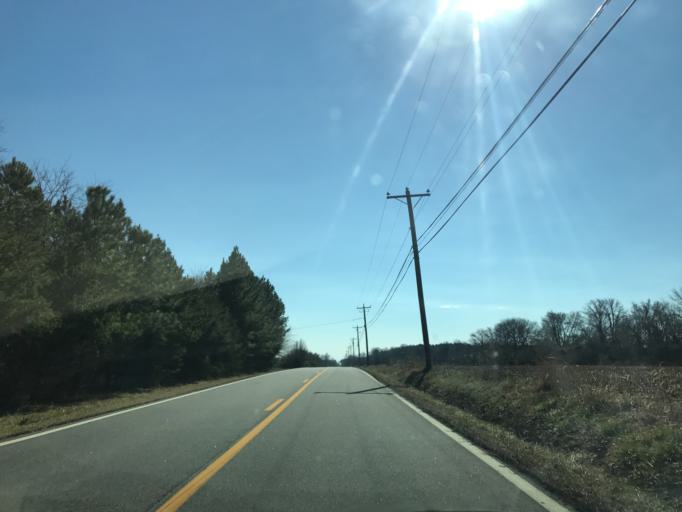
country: US
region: Maryland
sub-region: Queen Anne's County
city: Stevensville
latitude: 39.0220
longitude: -76.3113
